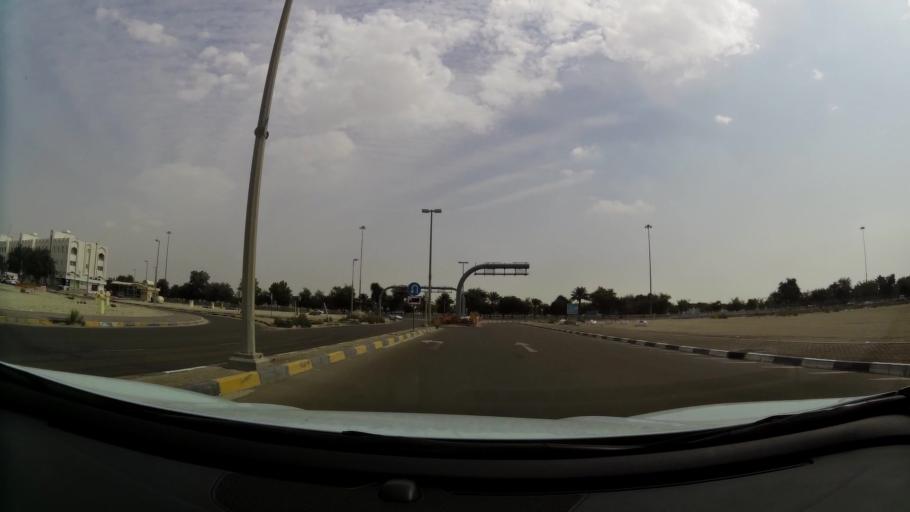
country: AE
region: Abu Dhabi
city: Abu Dhabi
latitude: 24.5228
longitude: 54.6896
